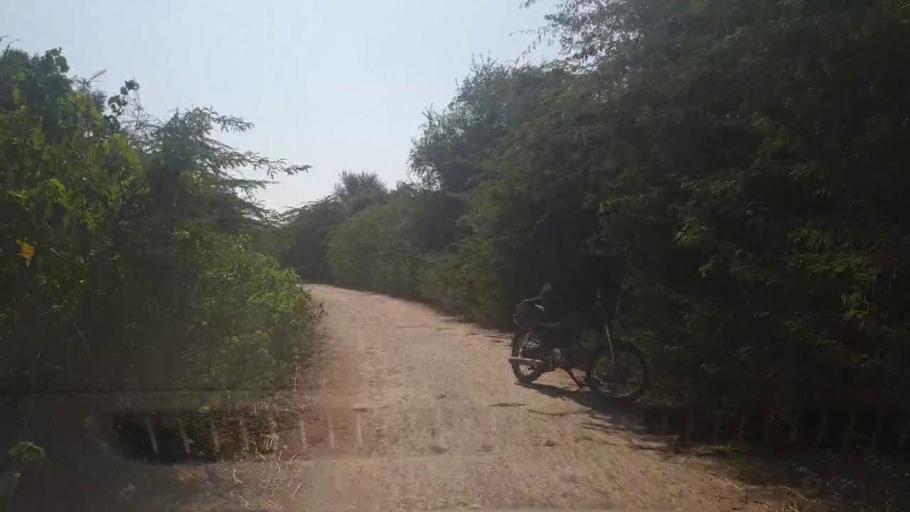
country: PK
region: Sindh
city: Badin
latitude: 24.6811
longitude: 68.8792
